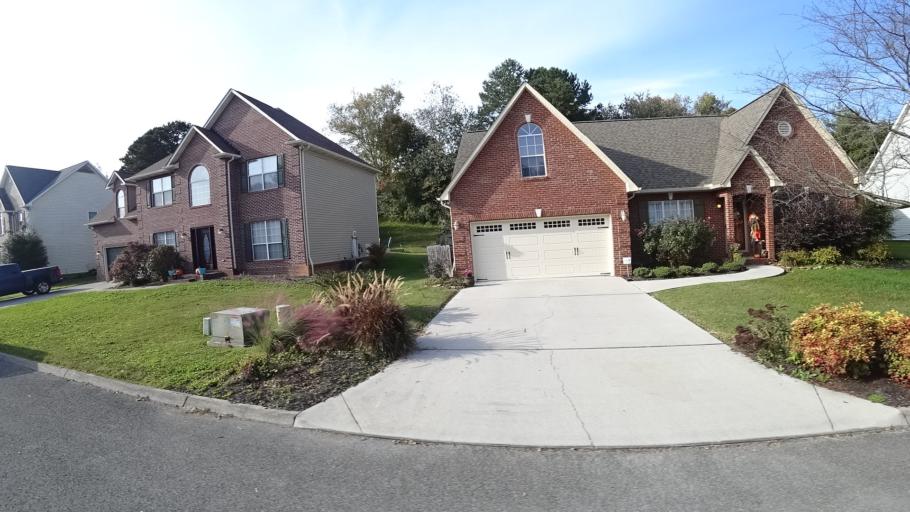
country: US
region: Tennessee
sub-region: Knox County
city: Farragut
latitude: 35.9097
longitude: -84.1639
